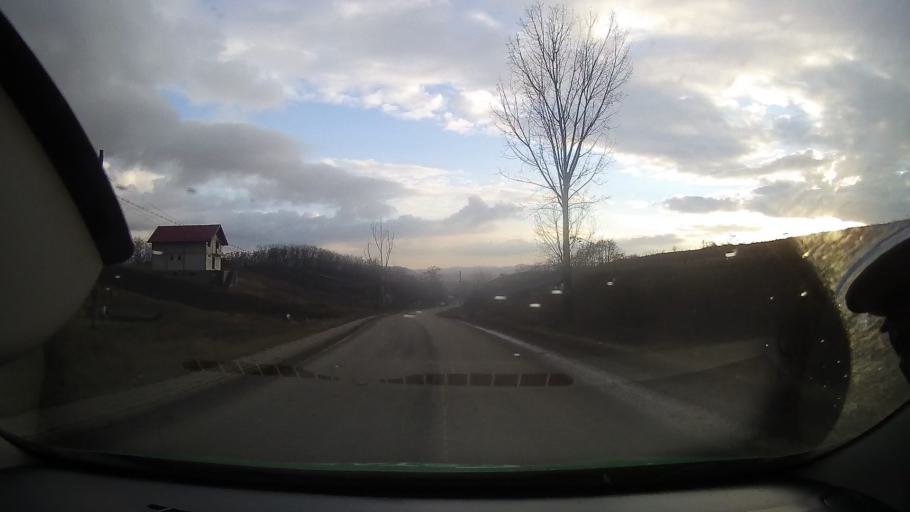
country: RO
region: Alba
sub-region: Comuna Lunca Muresului
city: Lunca Muresului
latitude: 46.4369
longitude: 23.9087
